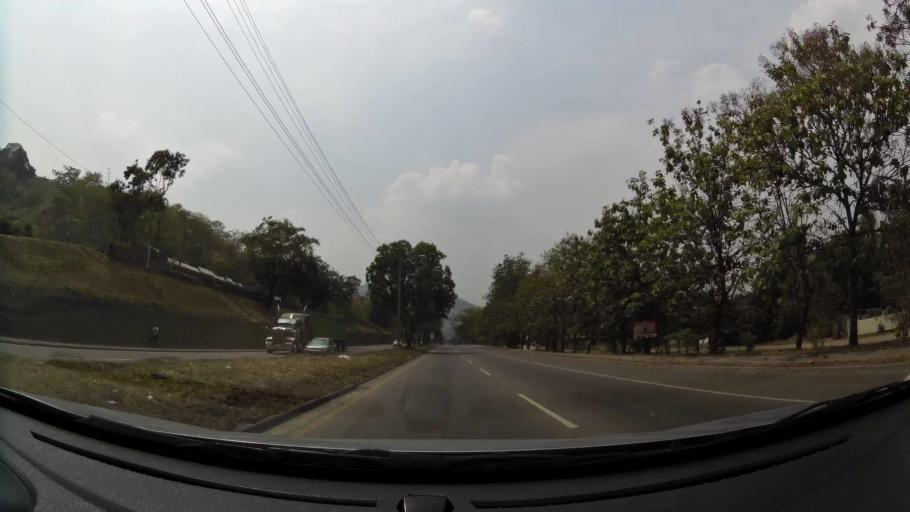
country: HN
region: Cortes
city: Chotepe
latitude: 15.4161
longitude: -88.0158
